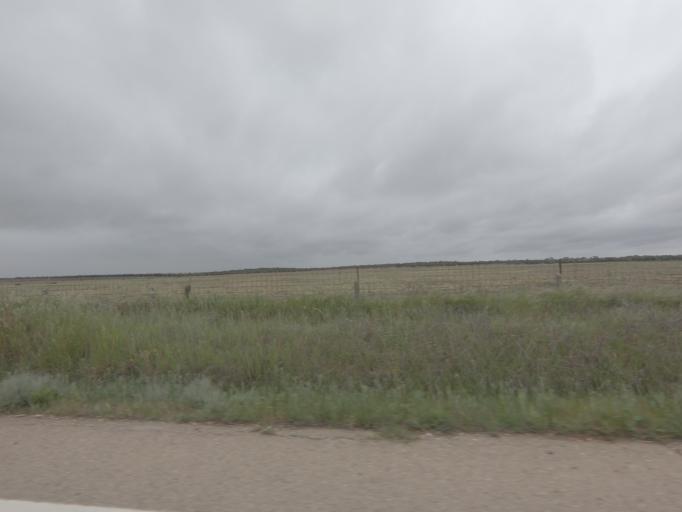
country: ES
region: Extremadura
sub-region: Provincia de Badajoz
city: Badajoz
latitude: 38.9745
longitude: -6.8899
